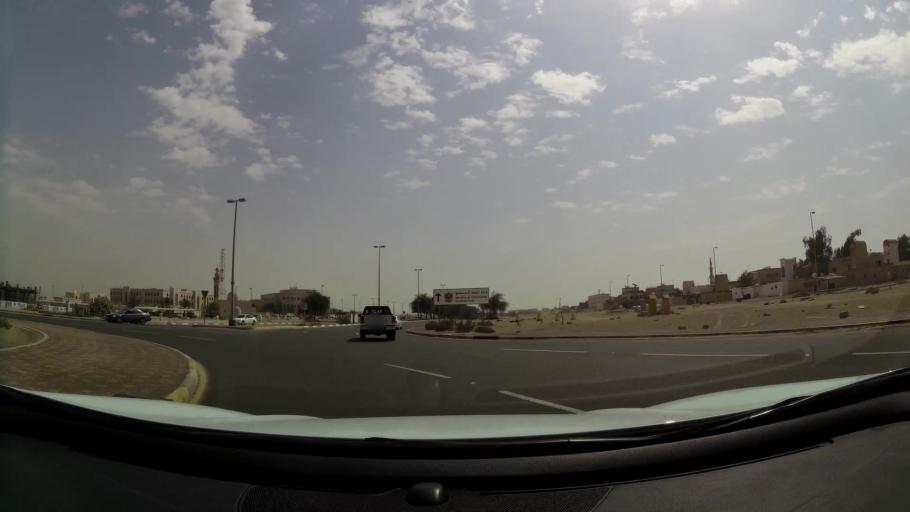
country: AE
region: Abu Dhabi
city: Abu Dhabi
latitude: 24.3148
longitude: 54.6080
